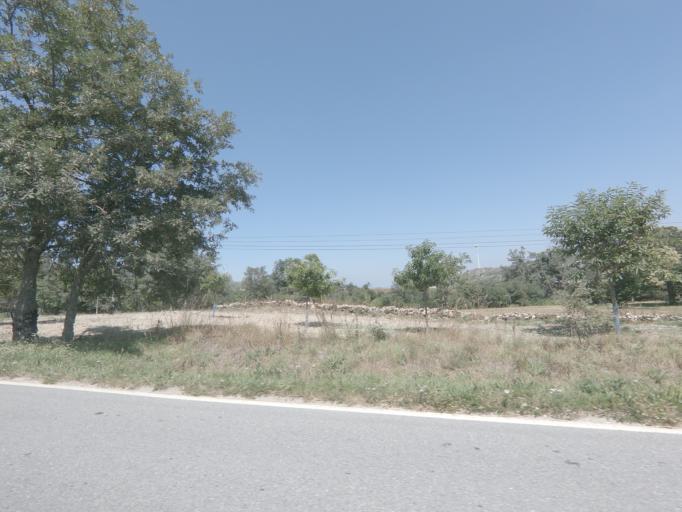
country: PT
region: Viseu
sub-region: Tarouca
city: Tarouca
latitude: 41.0008
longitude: -7.8870
